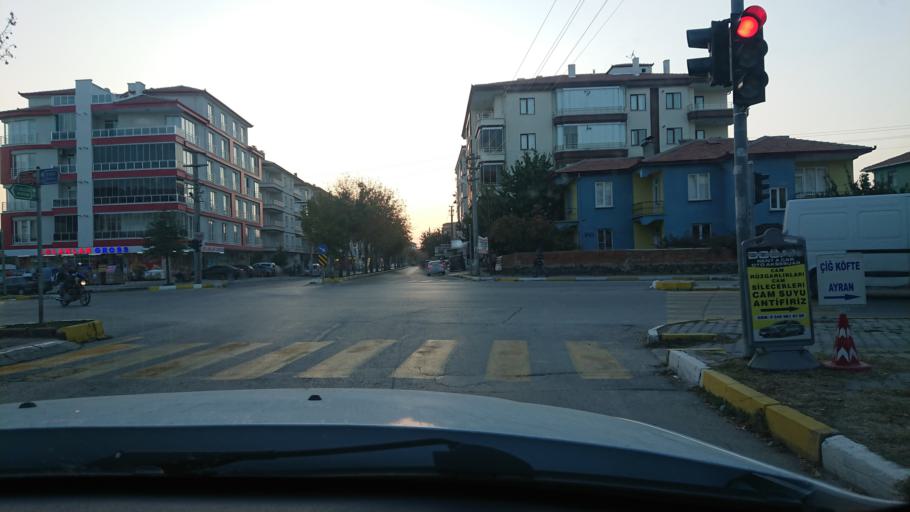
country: TR
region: Aksaray
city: Aksaray
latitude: 38.3625
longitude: 34.0302
